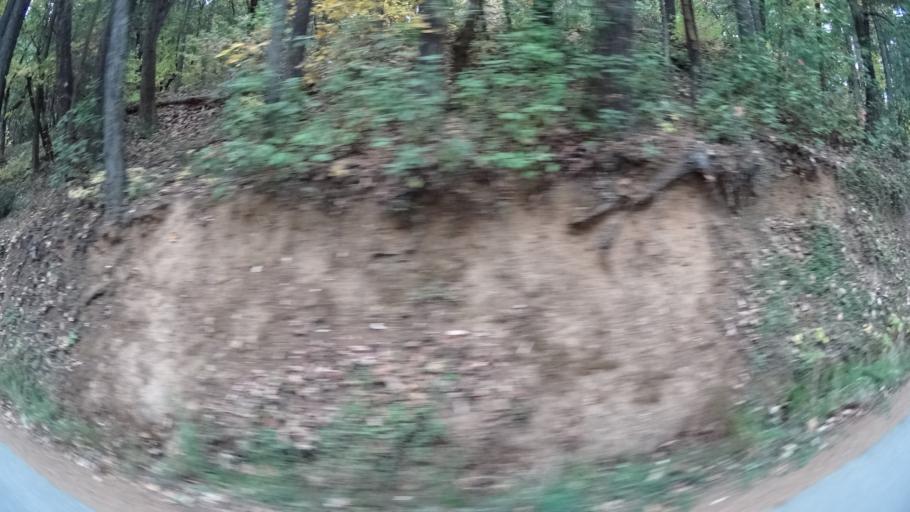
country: US
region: California
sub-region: Siskiyou County
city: Happy Camp
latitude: 41.8002
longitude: -123.3817
